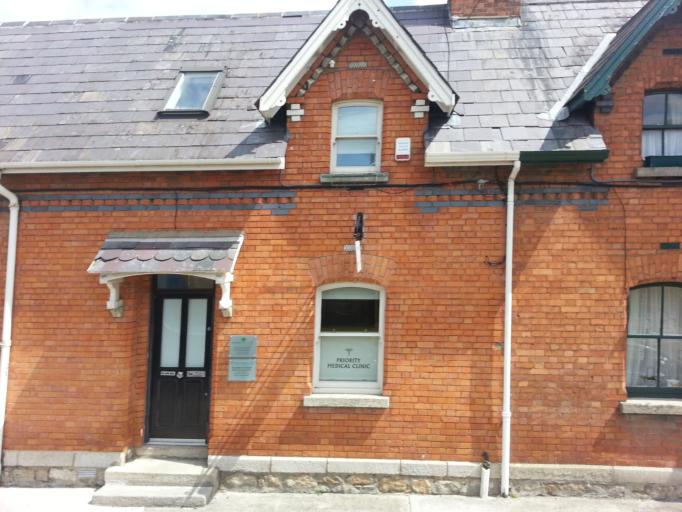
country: IE
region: Leinster
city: Dundrum
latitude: 53.2898
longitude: -6.2441
